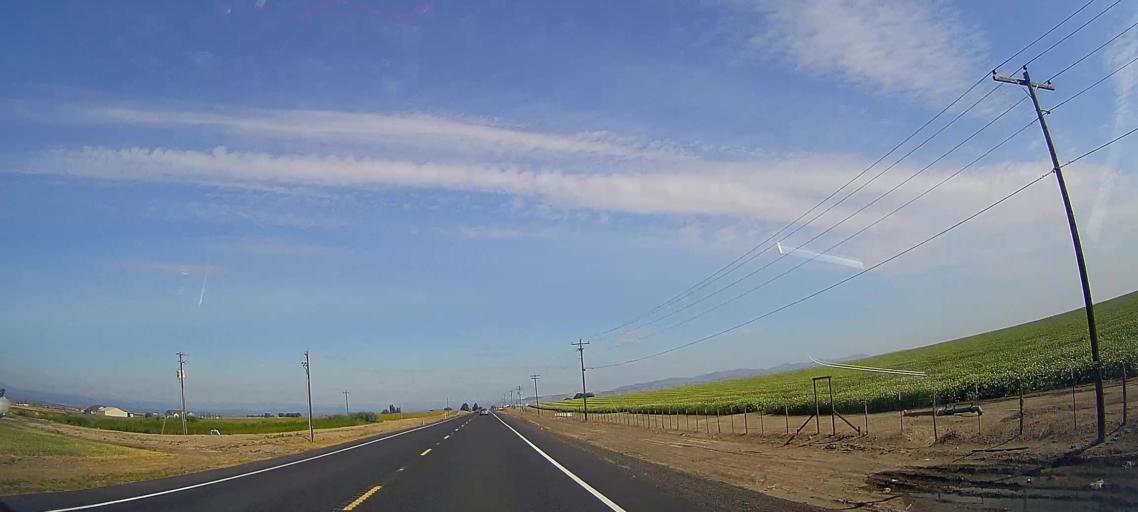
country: US
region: Oregon
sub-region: Jefferson County
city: Madras
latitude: 44.6821
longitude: -121.1484
